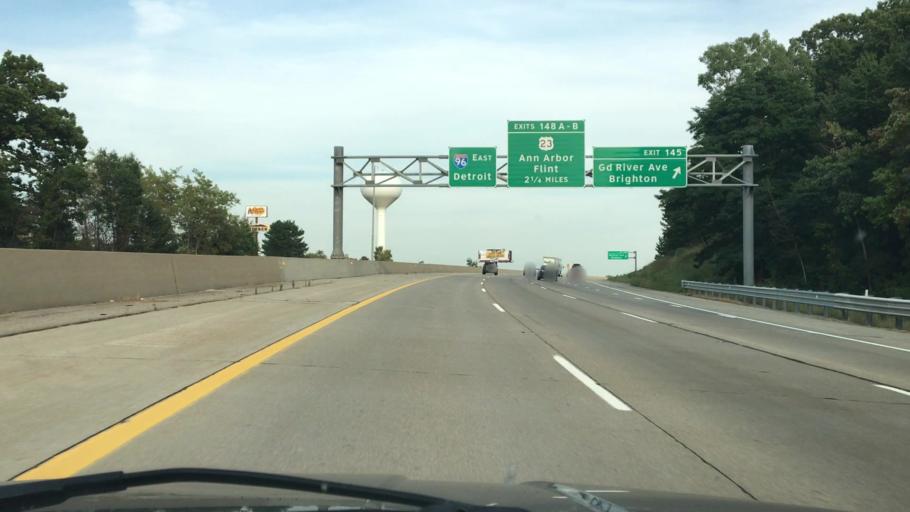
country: US
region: Michigan
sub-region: Livingston County
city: Brighton
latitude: 42.5512
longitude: -83.7984
